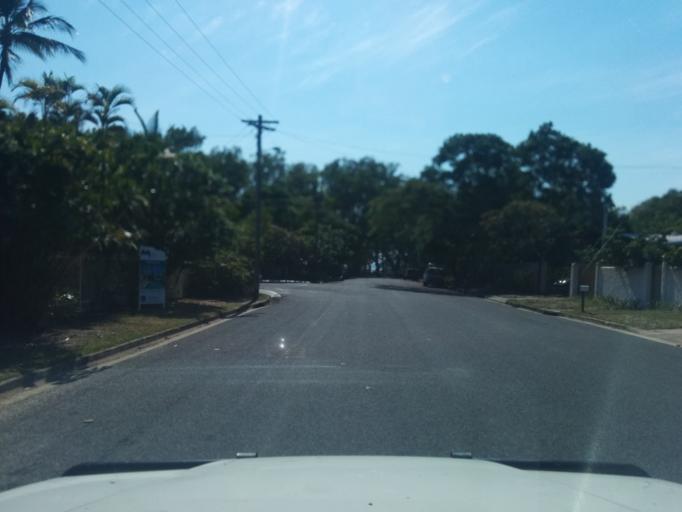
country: AU
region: Queensland
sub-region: Cairns
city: Yorkeys Knob
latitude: -16.8444
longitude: 145.7426
